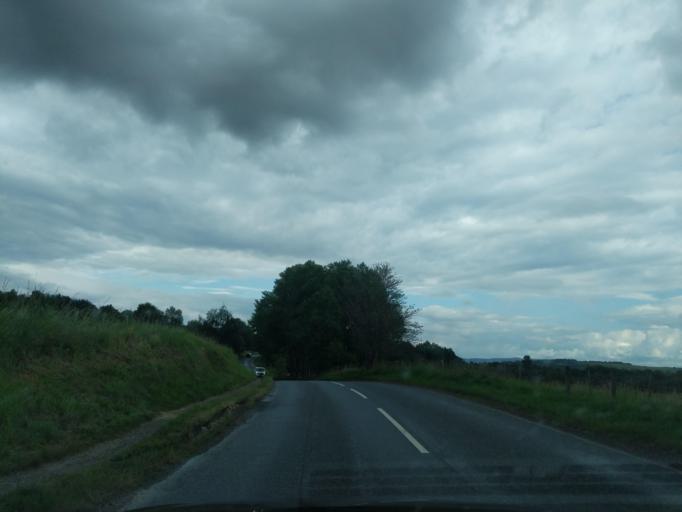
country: GB
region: Scotland
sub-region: Highland
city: Aviemore
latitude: 57.2861
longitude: -3.8085
